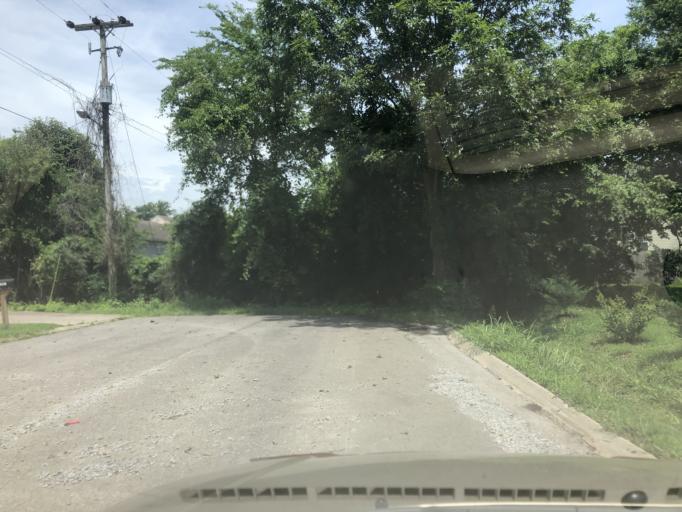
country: US
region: Tennessee
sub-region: Davidson County
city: Lakewood
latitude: 36.2496
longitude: -86.6749
